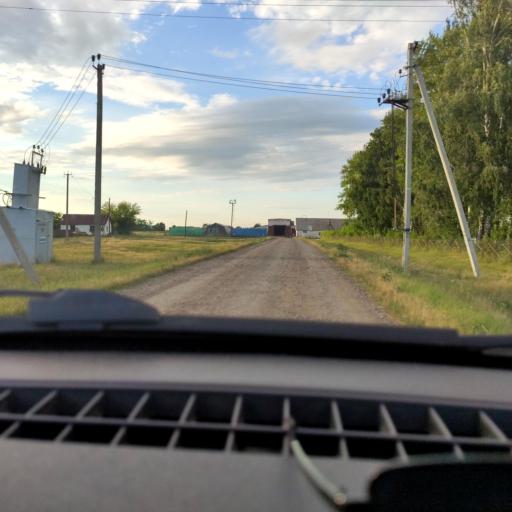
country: RU
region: Bashkortostan
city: Chishmy
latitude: 54.3759
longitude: 55.4210
